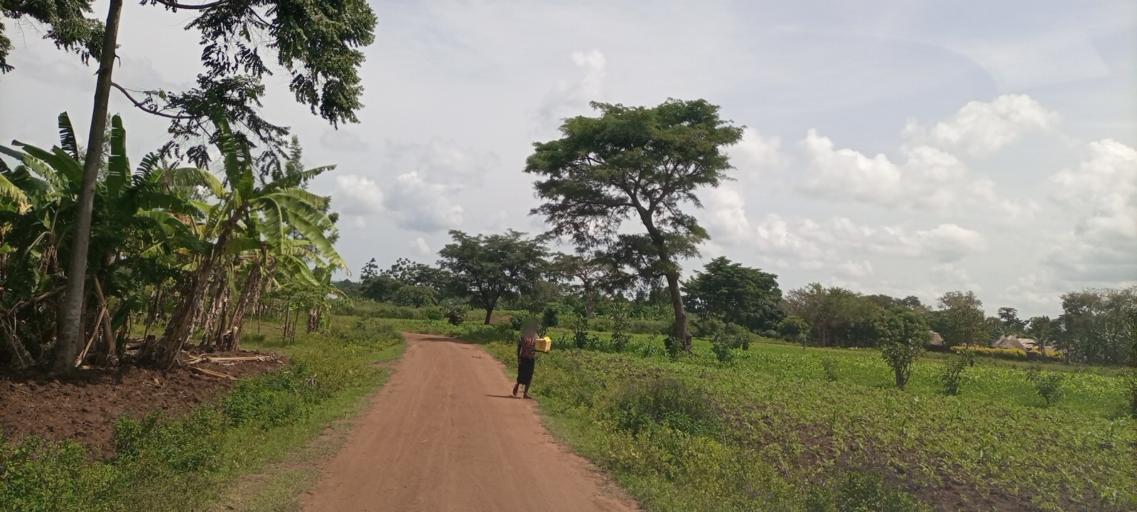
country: UG
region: Eastern Region
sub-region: Budaka District
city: Budaka
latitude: 1.1769
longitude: 33.9225
